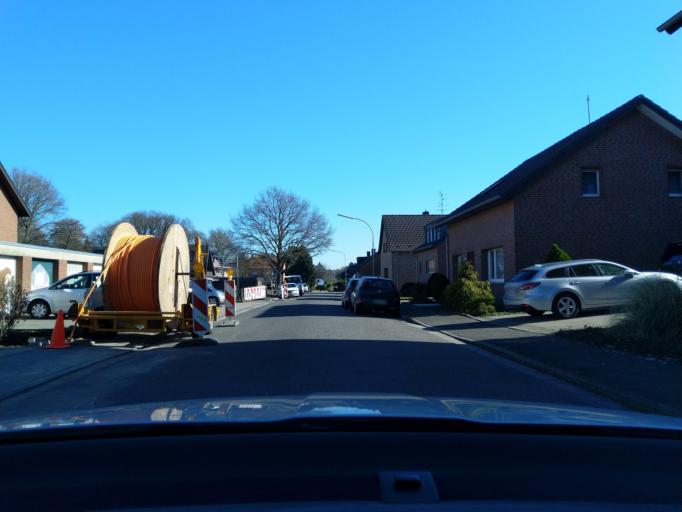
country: DE
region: North Rhine-Westphalia
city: Wegberg
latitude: 51.1493
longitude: 6.2748
